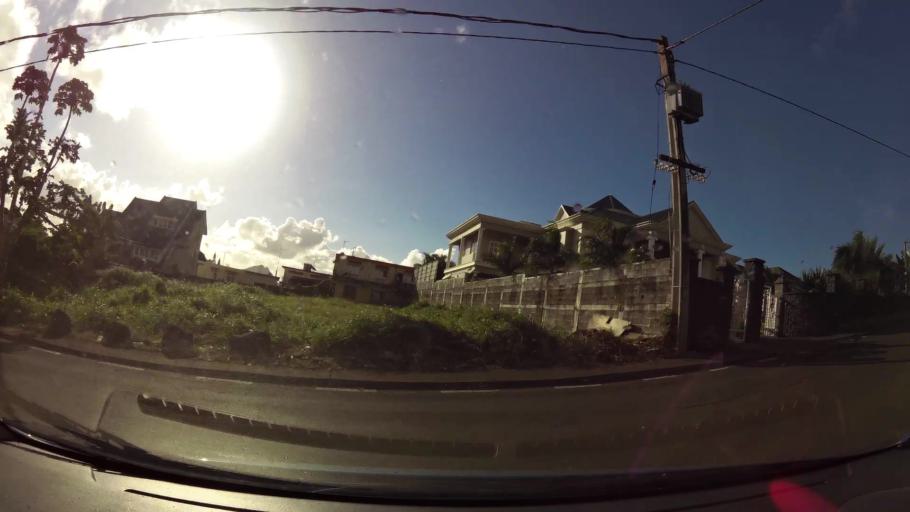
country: MU
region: Plaines Wilhems
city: Vacoas
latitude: -20.3084
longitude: 57.4958
